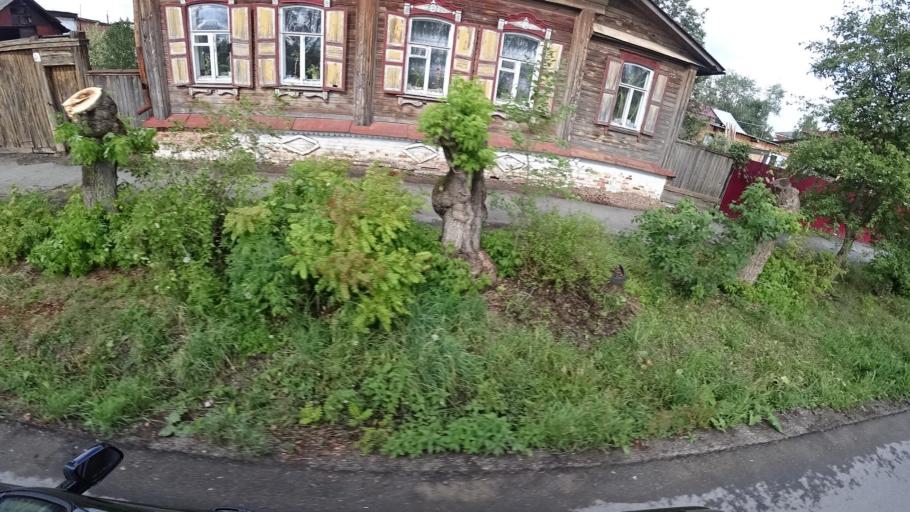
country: RU
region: Sverdlovsk
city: Kamyshlov
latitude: 56.8413
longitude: 62.7029
